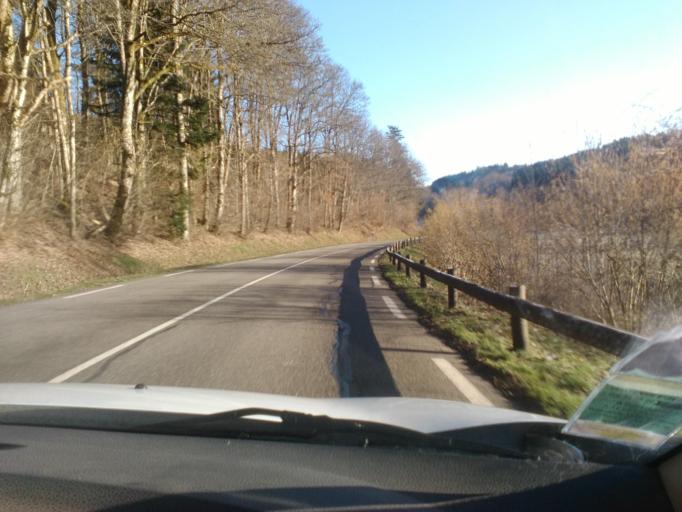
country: FR
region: Alsace
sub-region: Departement du Haut-Rhin
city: Sainte-Marie-aux-Mines
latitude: 48.3544
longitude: 7.1318
